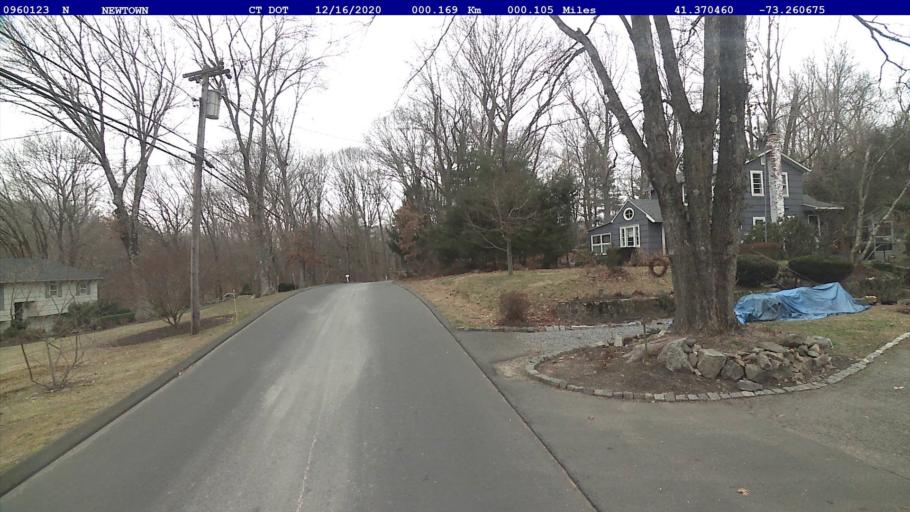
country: US
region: Connecticut
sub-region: Fairfield County
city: Newtown
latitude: 41.3705
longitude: -73.2607
